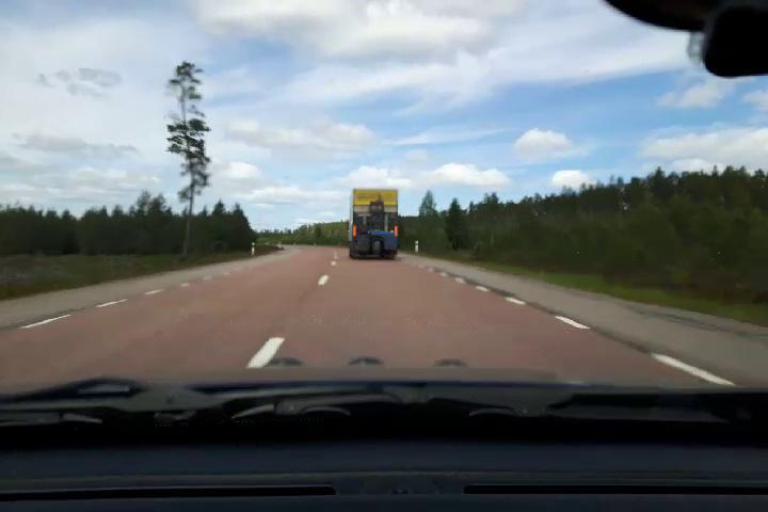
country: SE
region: Uppsala
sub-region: Osthammars Kommun
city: Bjorklinge
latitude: 60.1655
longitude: 17.4914
